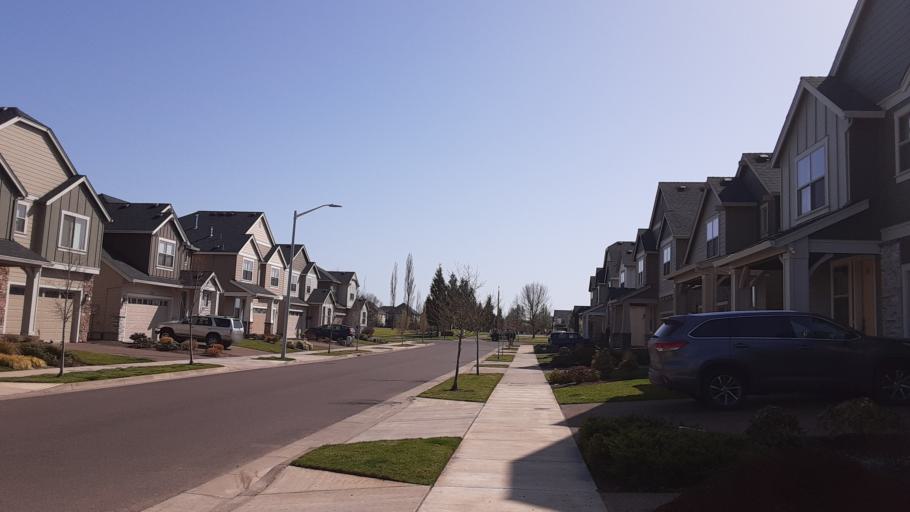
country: US
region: Oregon
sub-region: Benton County
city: Corvallis
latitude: 44.5320
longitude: -123.2608
